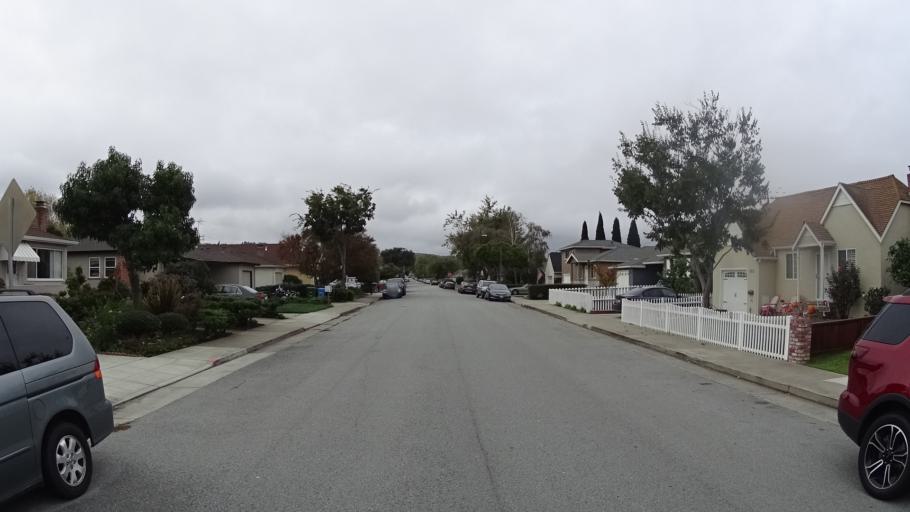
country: US
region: California
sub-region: San Mateo County
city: Foster City
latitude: 37.5416
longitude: -122.2889
